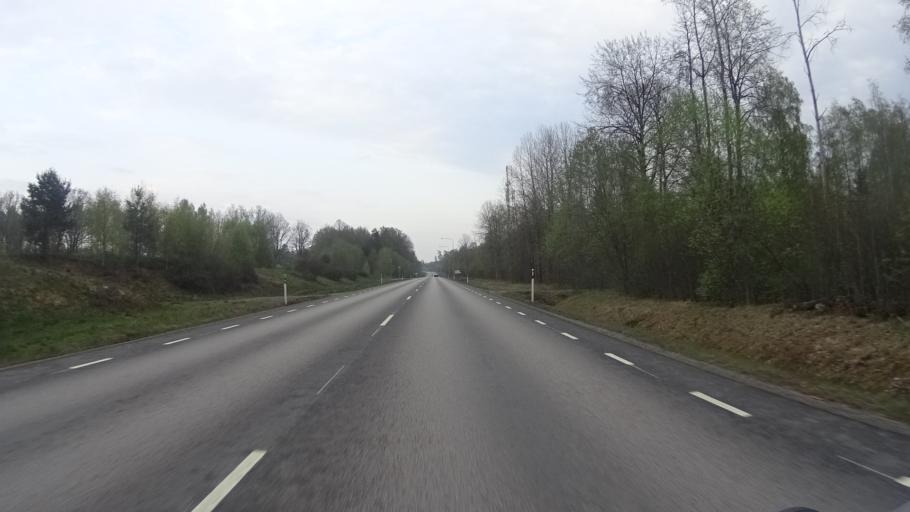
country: SE
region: Kronoberg
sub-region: Ljungby Kommun
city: Ljungby
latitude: 56.8213
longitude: 13.9526
